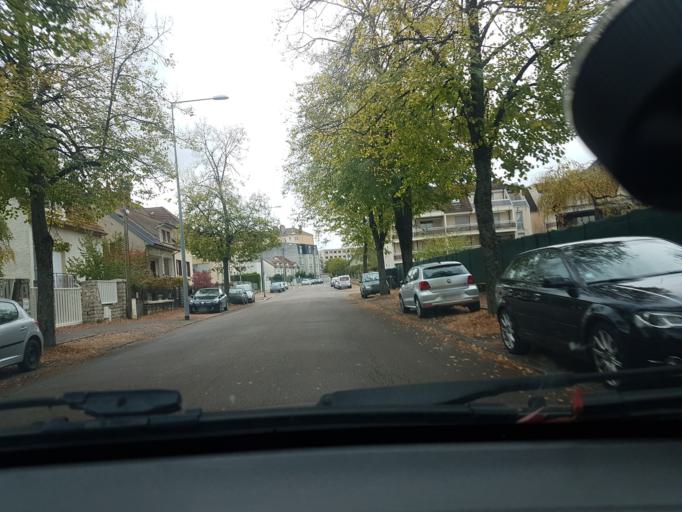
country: FR
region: Bourgogne
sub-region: Departement de la Cote-d'Or
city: Longvic
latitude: 47.3111
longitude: 5.0575
